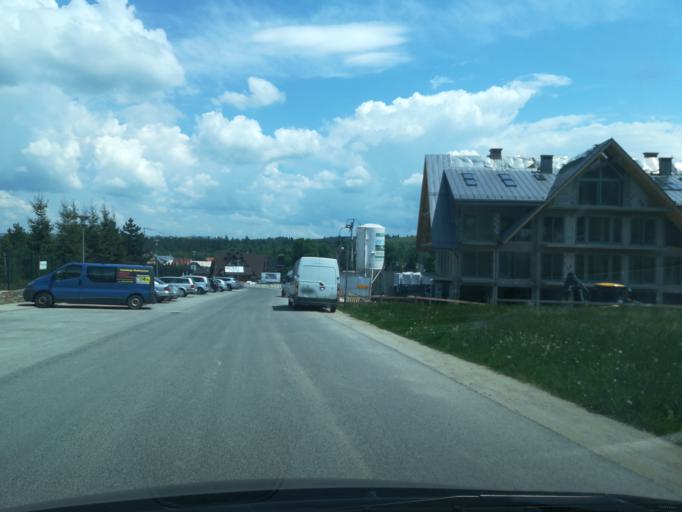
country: PL
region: Lesser Poland Voivodeship
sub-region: Powiat tatrzanski
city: Bialka Tatrzanska
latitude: 49.3869
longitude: 20.0993
